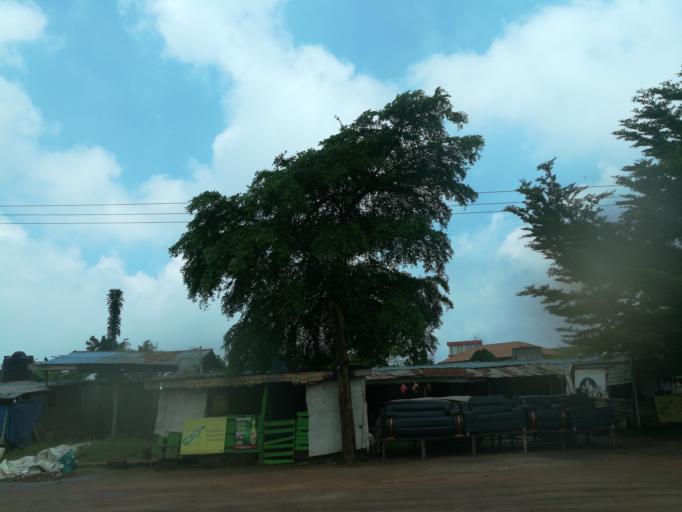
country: NG
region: Lagos
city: Ikorodu
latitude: 6.6703
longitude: 3.5126
